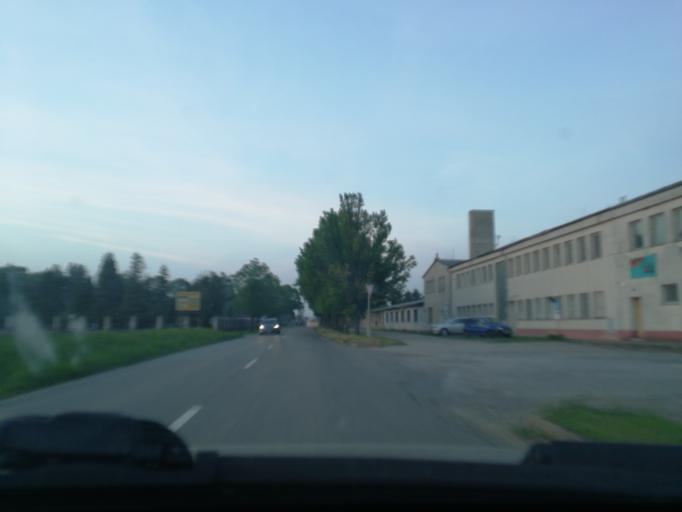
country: CZ
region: Zlin
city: Holesov
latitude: 49.3014
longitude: 17.5582
